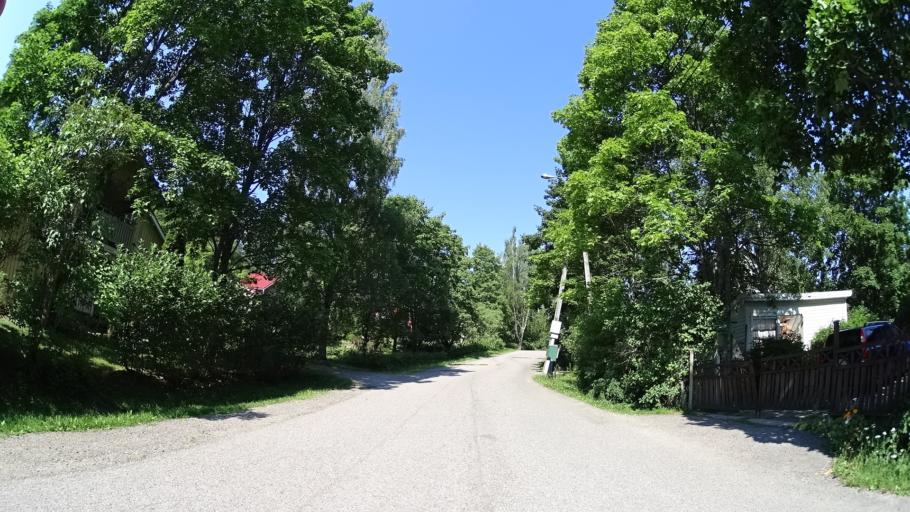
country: FI
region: Uusimaa
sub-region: Helsinki
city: Kerava
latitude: 60.3738
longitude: 25.0851
